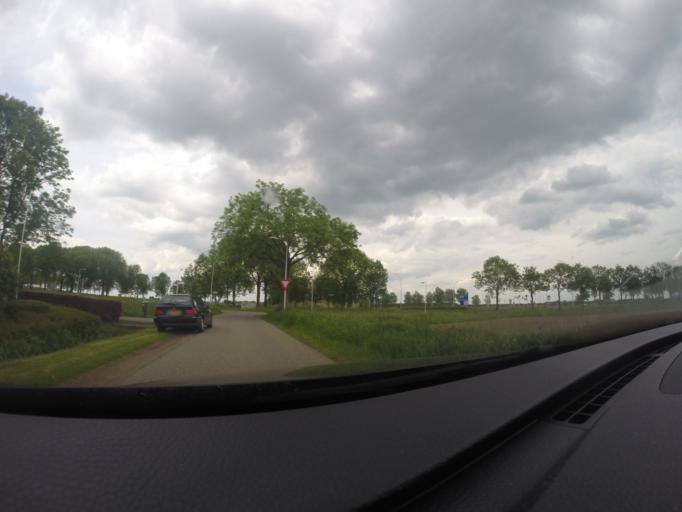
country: NL
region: Gelderland
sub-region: Gemeente Hattem
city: Hattem
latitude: 52.5297
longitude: 6.0303
